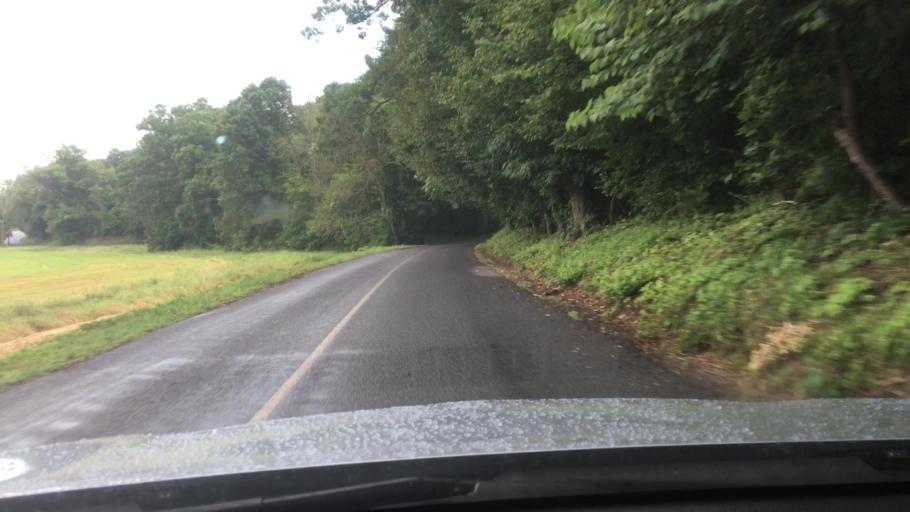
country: US
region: Pennsylvania
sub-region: Franklin County
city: Greencastle
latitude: 39.8692
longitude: -77.7882
